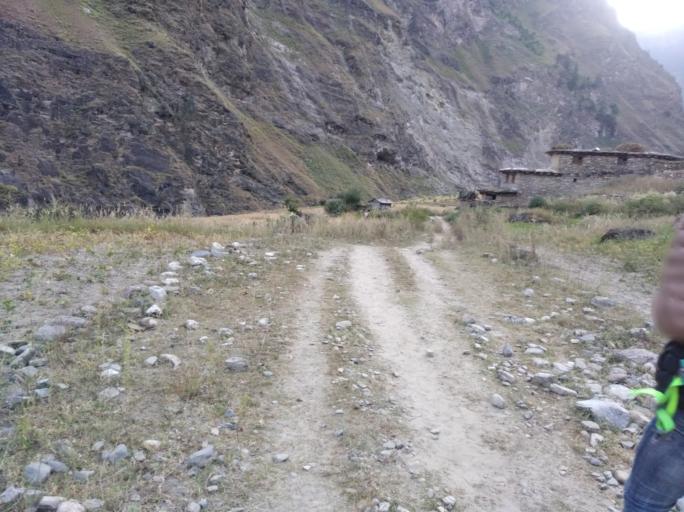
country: NP
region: Western Region
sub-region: Dhawalagiri Zone
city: Jomsom
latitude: 28.8805
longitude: 82.9925
